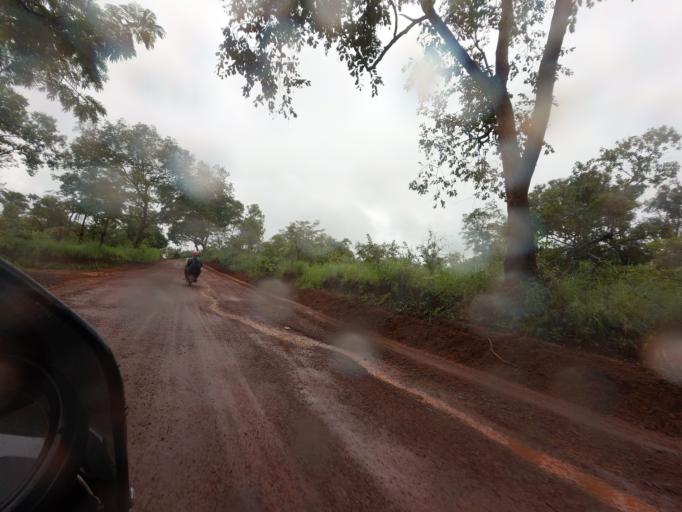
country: SL
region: Northern Province
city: Kambia
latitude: 9.2159
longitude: -12.8544
